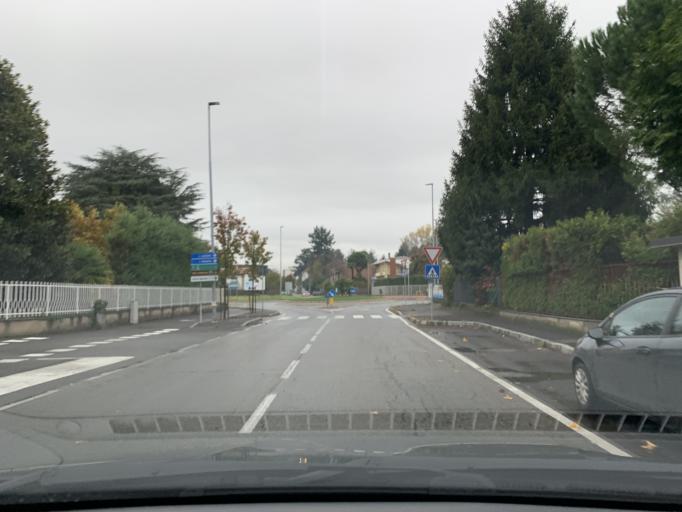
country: IT
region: Lombardy
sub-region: Provincia di Como
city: Rovellasca
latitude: 45.6602
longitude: 9.0534
